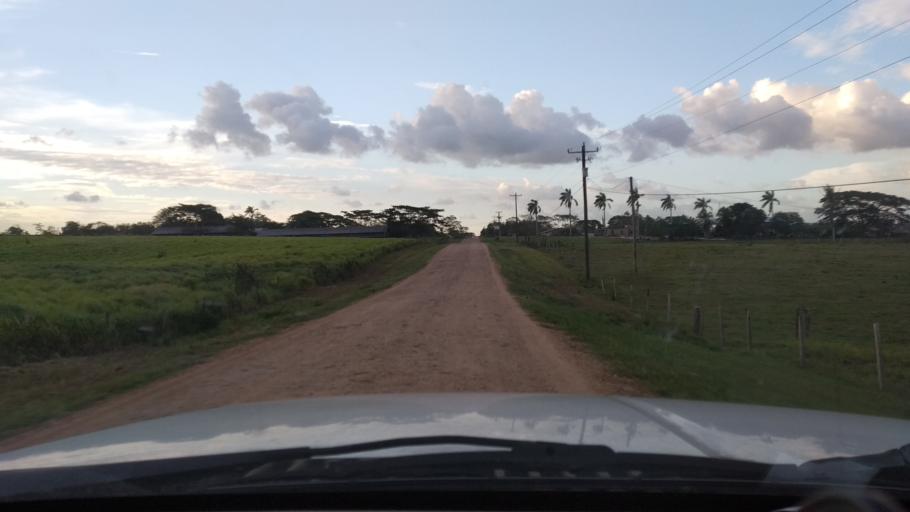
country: BZ
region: Cayo
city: San Ignacio
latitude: 17.2293
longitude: -88.9876
